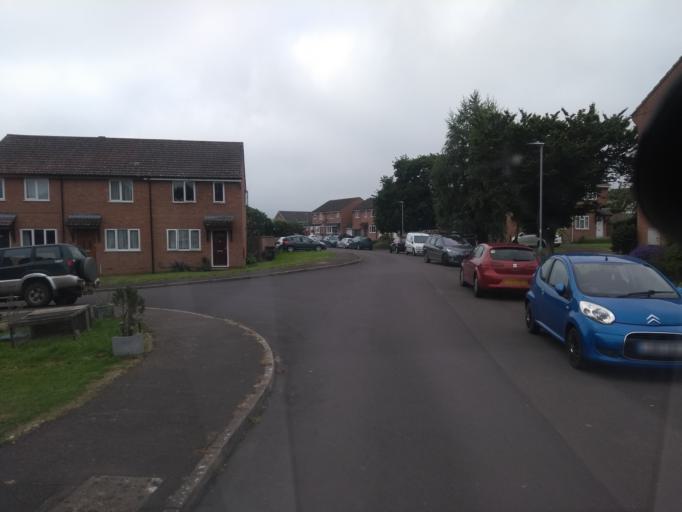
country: GB
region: England
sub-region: Somerset
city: Chard
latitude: 50.8814
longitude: -2.9595
